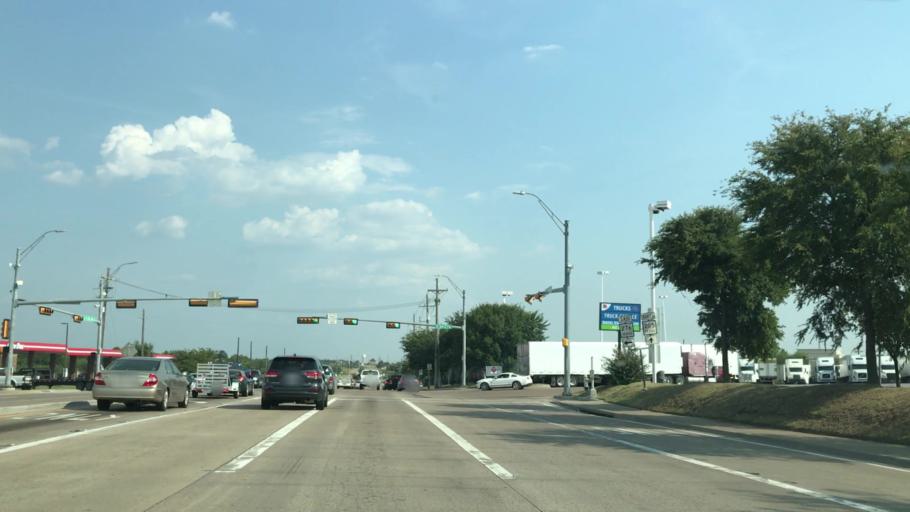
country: US
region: Texas
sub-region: Rockwall County
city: Rockwall
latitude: 32.9075
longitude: -96.4490
